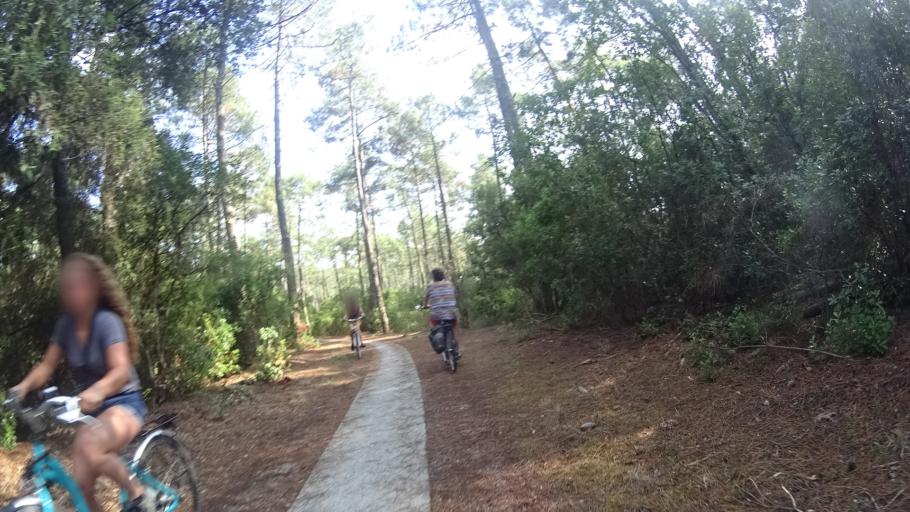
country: FR
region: Aquitaine
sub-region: Departement de la Gironde
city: Lacanau
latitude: 44.9636
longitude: -1.1731
